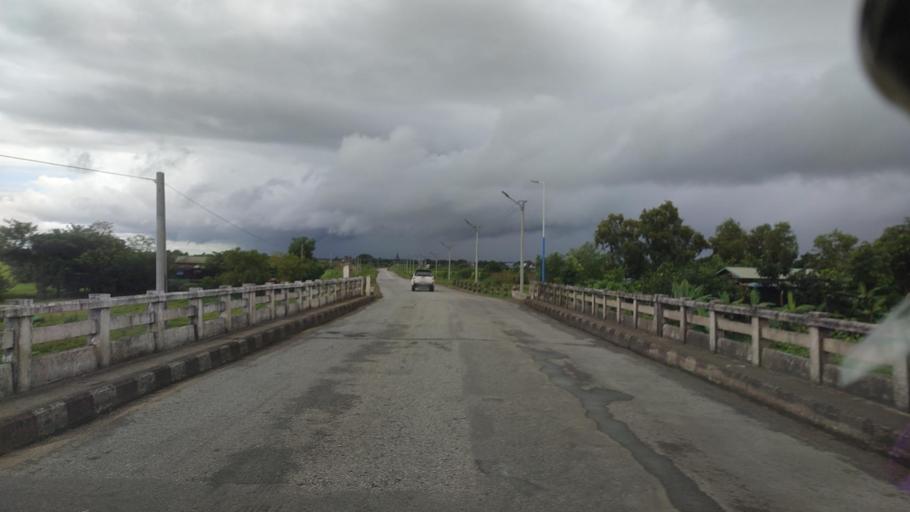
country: MM
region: Bago
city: Bago
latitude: 17.3828
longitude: 96.4815
